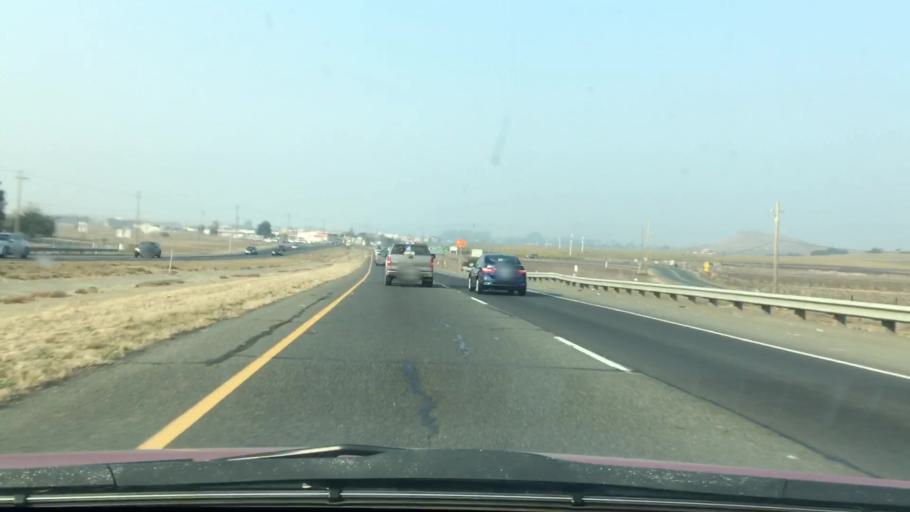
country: US
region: California
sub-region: Napa County
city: American Canyon
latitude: 38.1921
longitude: -122.2557
